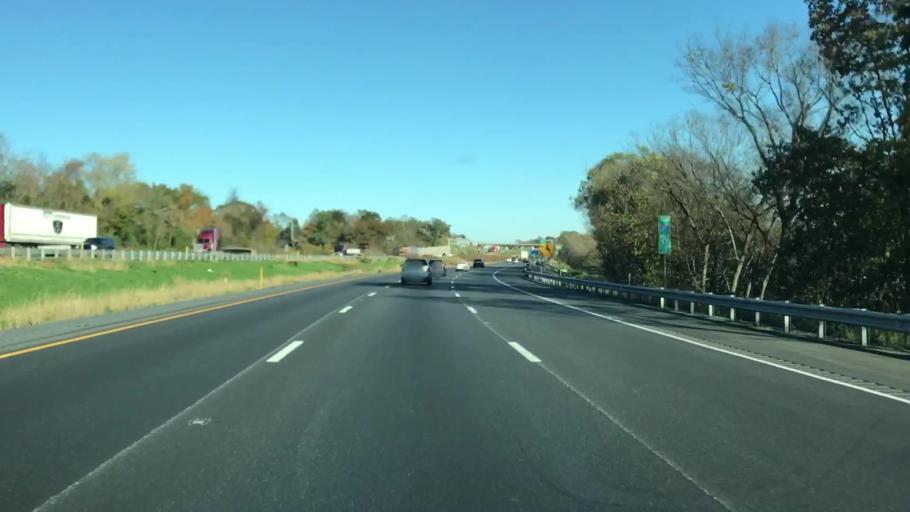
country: US
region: Pennsylvania
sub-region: Cumberland County
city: Mechanicsburg
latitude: 40.2714
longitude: -77.0366
